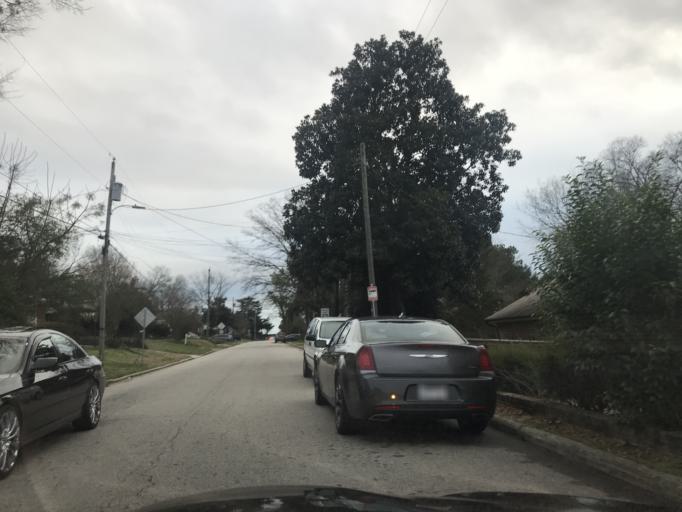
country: US
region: North Carolina
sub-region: Wake County
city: Raleigh
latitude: 35.7702
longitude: -78.6246
